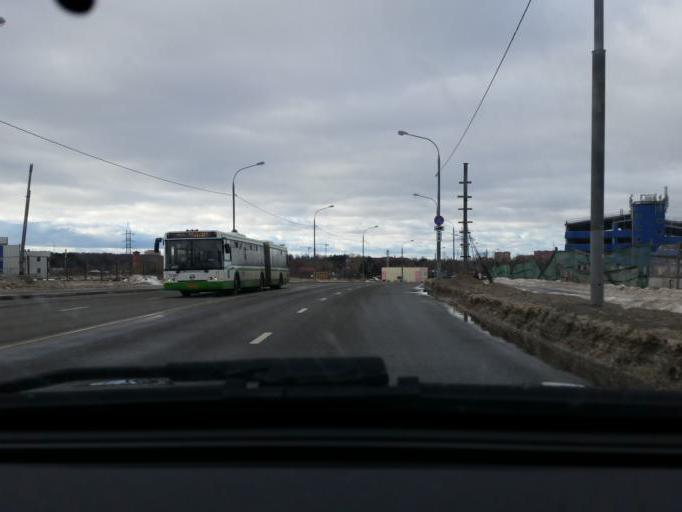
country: RU
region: Moskovskaya
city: Shcherbinka
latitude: 55.5009
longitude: 37.6004
